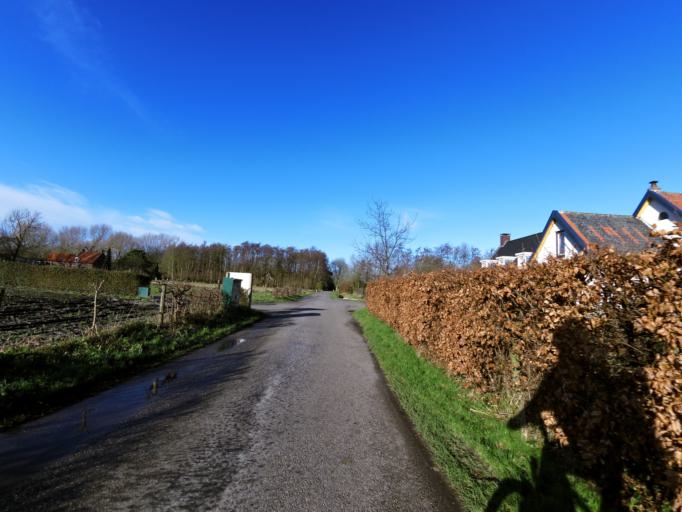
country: NL
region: South Holland
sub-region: Gemeente Hellevoetsluis
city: Nieuw-Helvoet
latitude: 51.8590
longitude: 4.0715
